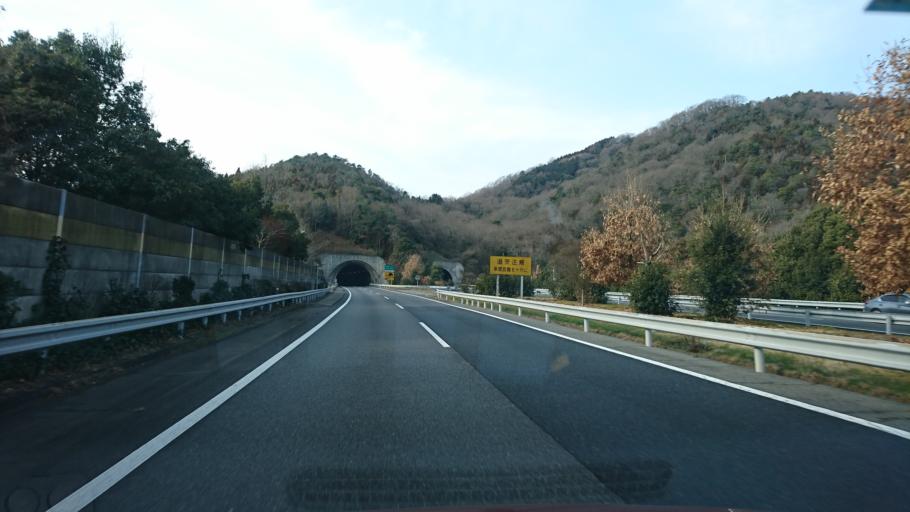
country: JP
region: Okayama
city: Okayama-shi
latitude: 34.7678
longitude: 134.0662
